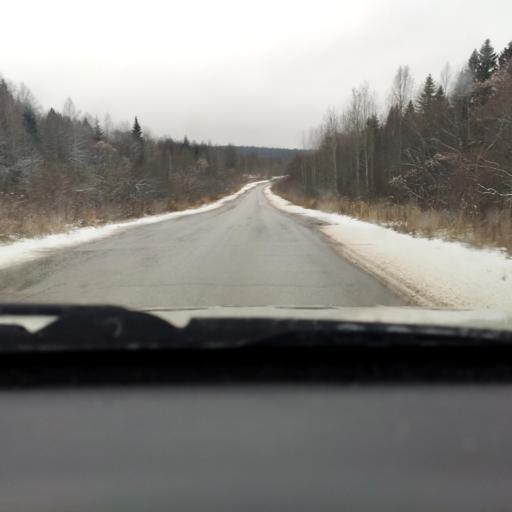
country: RU
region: Perm
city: Ferma
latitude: 57.9800
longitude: 56.3582
